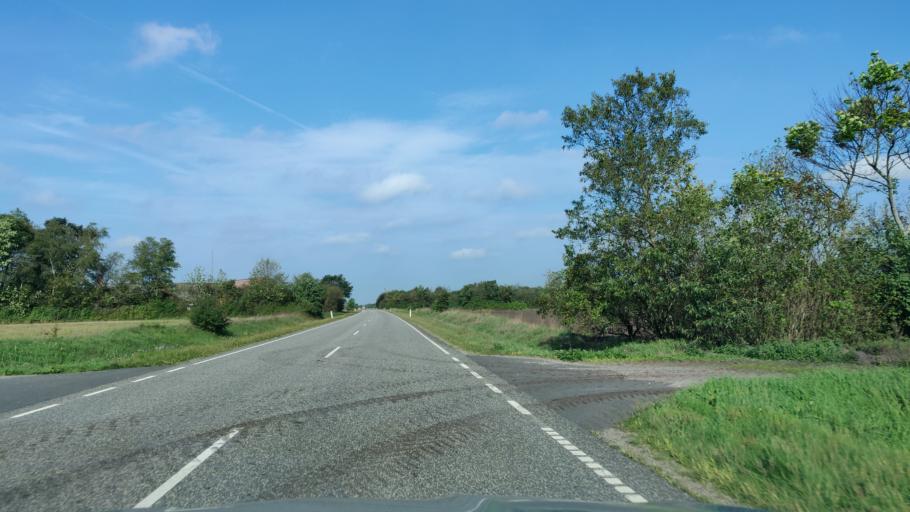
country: DK
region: Central Jutland
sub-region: Herning Kommune
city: Sunds
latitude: 56.2554
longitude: 9.0457
